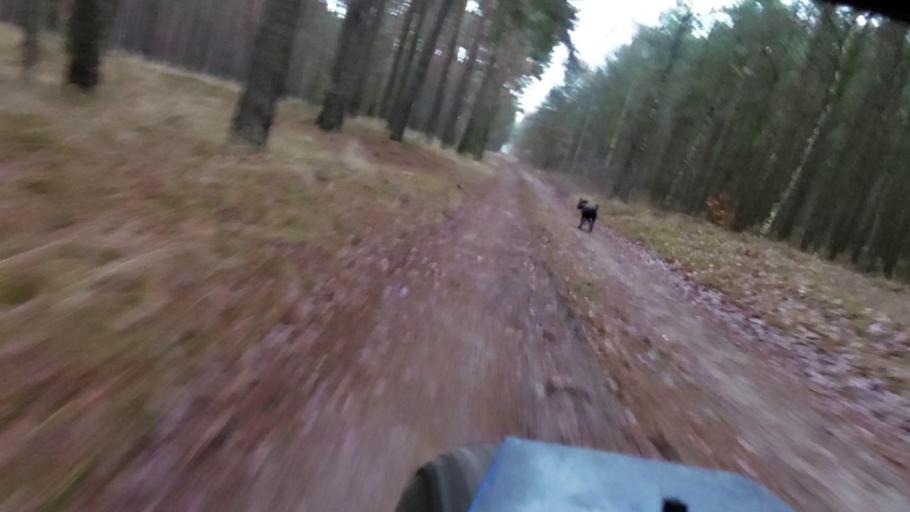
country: PL
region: Lubusz
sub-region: Powiat gorzowski
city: Witnica
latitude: 52.6963
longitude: 14.8154
